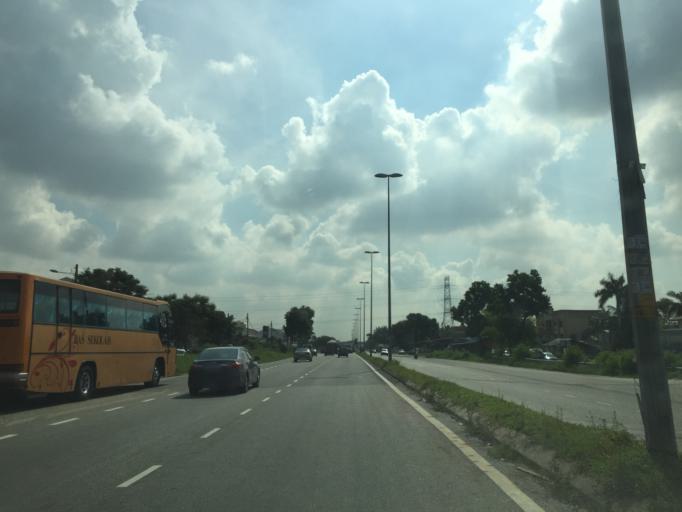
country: MY
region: Selangor
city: Klang
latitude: 3.0137
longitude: 101.4587
